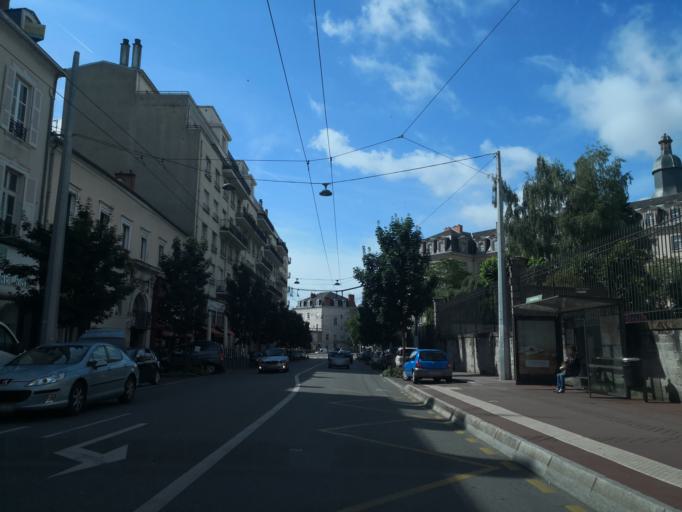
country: FR
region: Limousin
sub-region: Departement de la Haute-Vienne
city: Limoges
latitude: 45.8315
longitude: 1.2625
